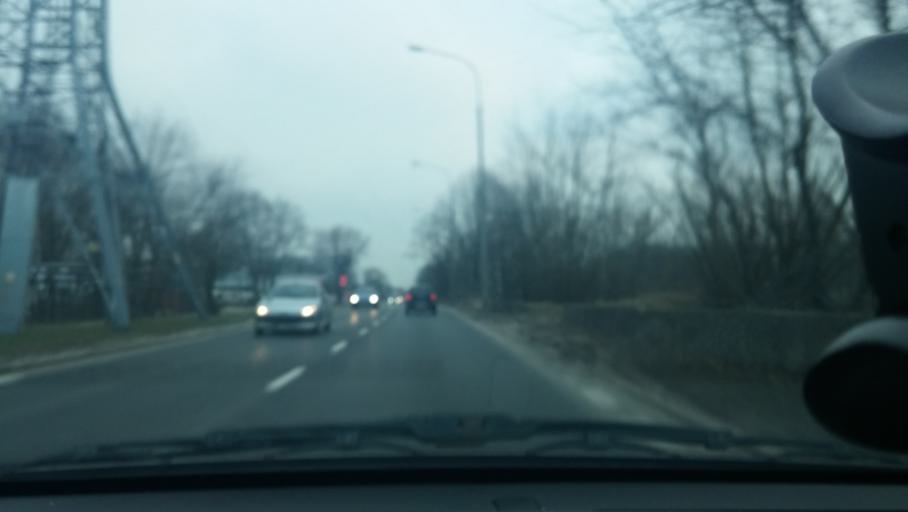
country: PL
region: Masovian Voivodeship
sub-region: Warszawa
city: Wawer
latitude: 52.2097
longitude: 21.1638
